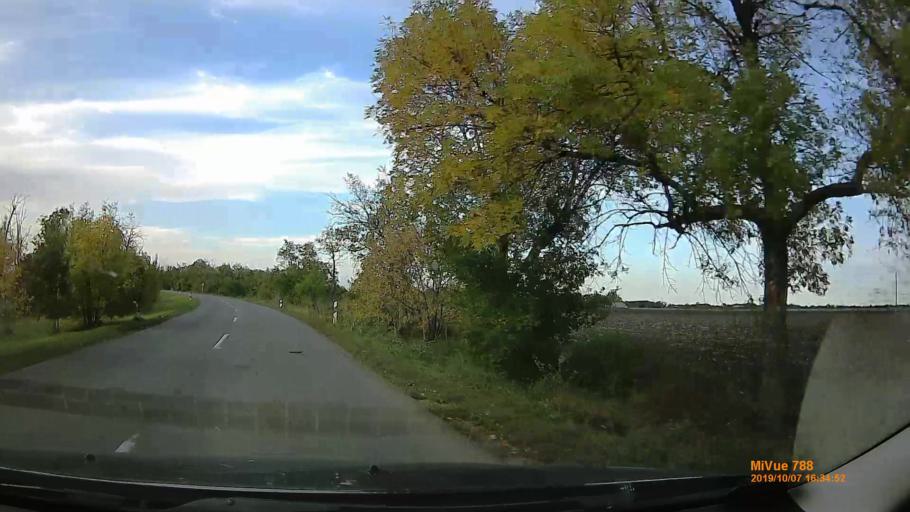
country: HU
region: Bekes
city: Szarvas
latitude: 46.8064
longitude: 20.6181
